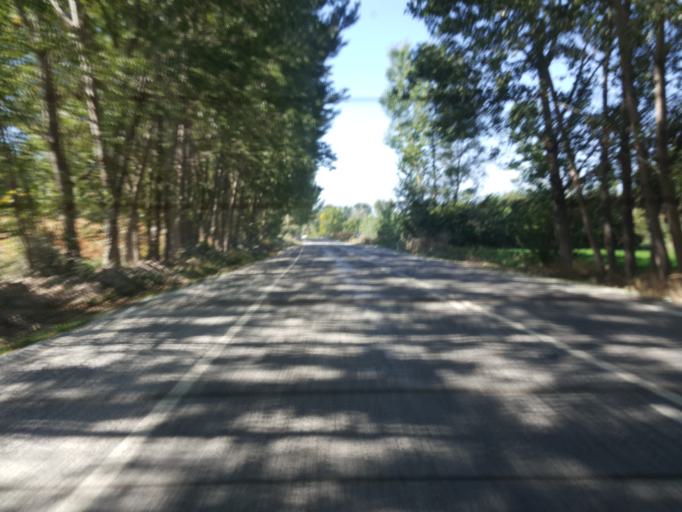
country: TR
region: Tokat
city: Pazar
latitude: 40.2740
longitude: 36.2624
